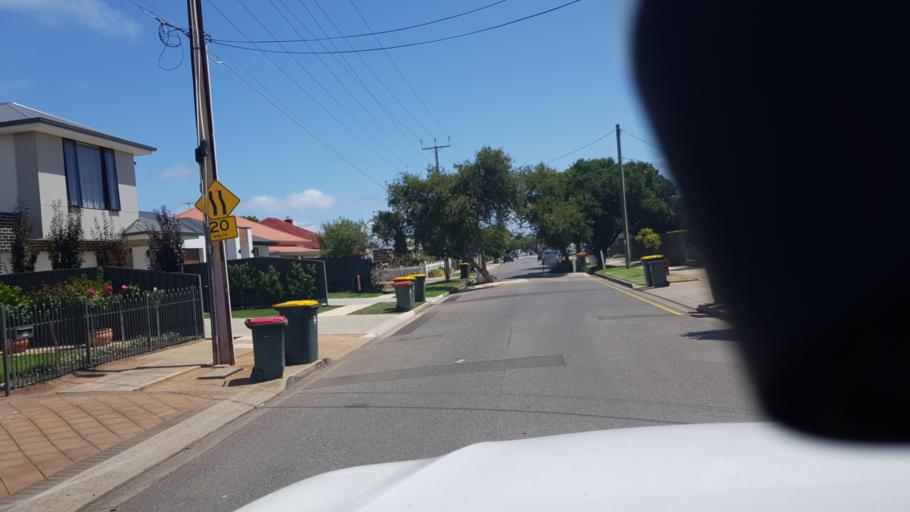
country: AU
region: South Australia
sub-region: Holdfast Bay
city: North Brighton
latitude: -34.9920
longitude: 138.5316
